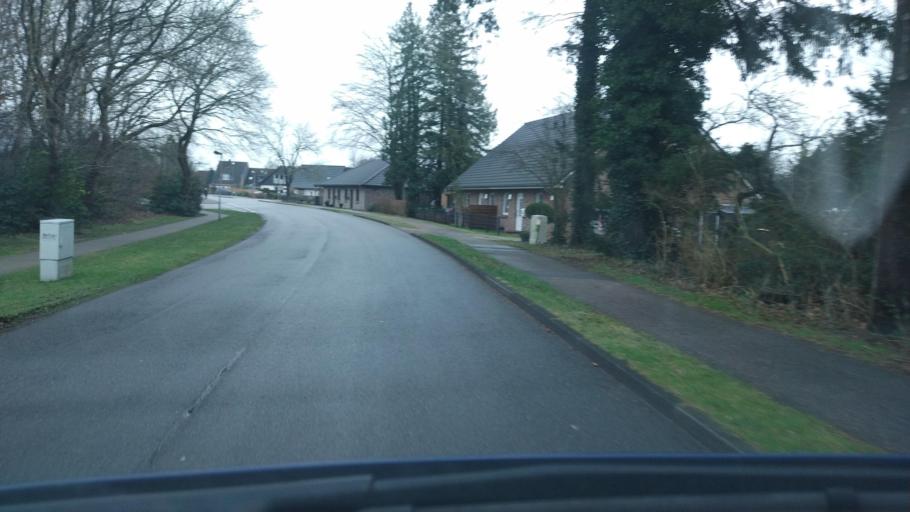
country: DE
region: Schleswig-Holstein
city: Kropp
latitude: 54.4083
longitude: 9.4992
